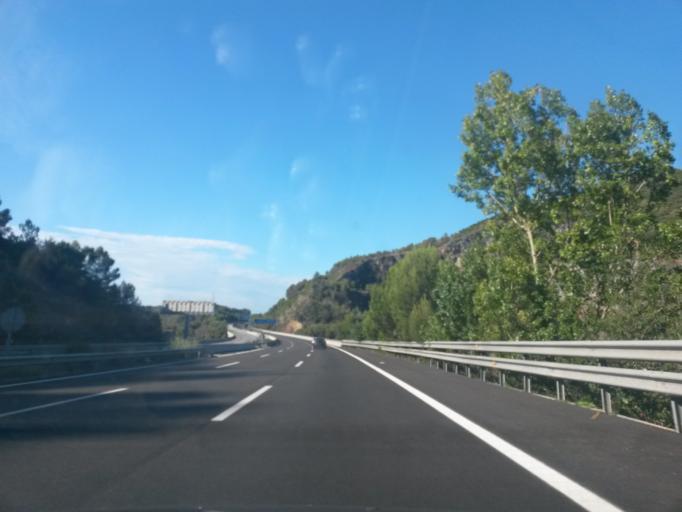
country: ES
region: Catalonia
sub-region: Provincia de Barcelona
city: Pineda de Mar
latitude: 41.6455
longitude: 2.6782
